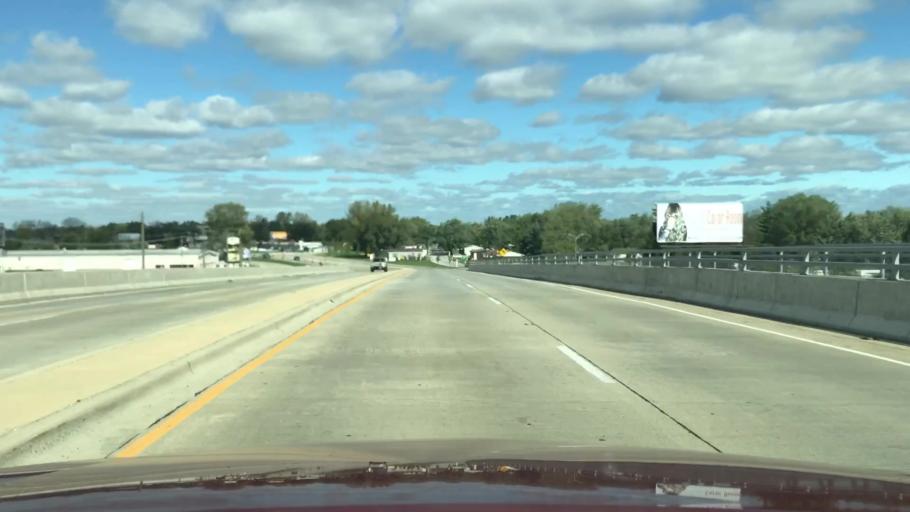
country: US
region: Indiana
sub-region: Lake County
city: Dyer
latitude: 41.4982
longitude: -87.5288
